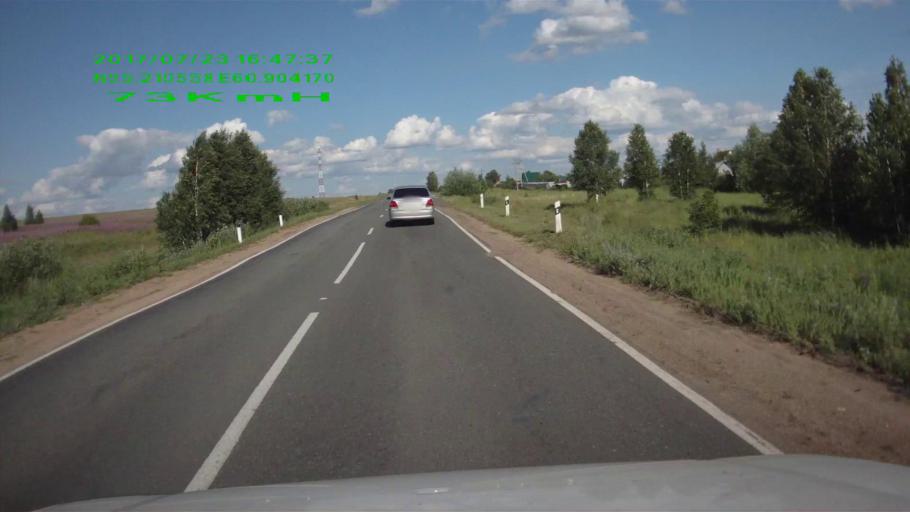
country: RU
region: Chelyabinsk
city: Poletayevo
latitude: 55.2106
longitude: 60.9041
